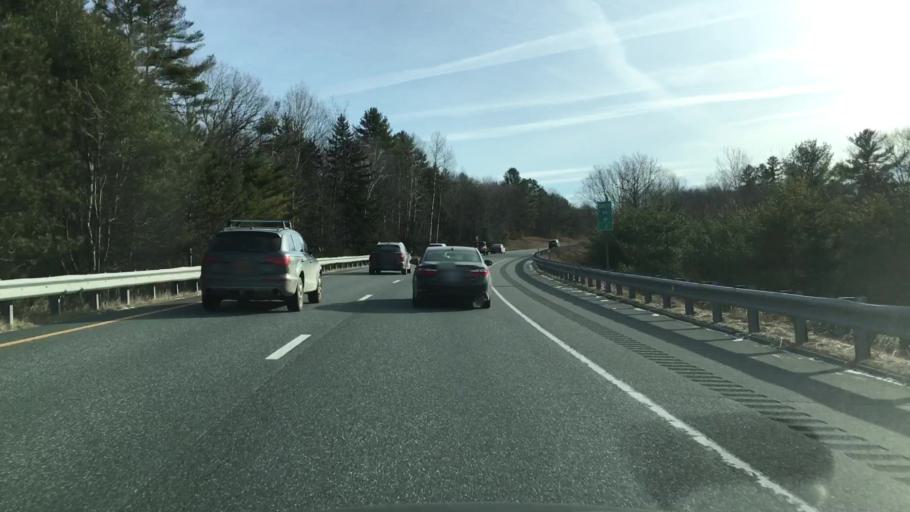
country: US
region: New Hampshire
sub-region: Sullivan County
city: Grantham
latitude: 43.4875
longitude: -72.1068
